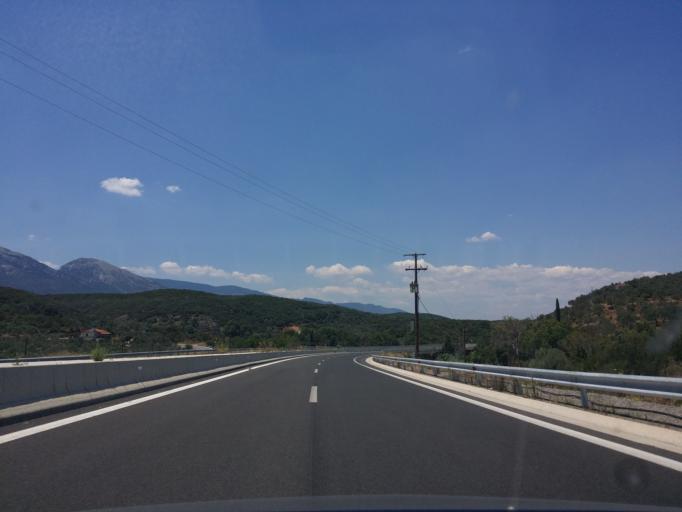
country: GR
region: Peloponnese
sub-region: Nomos Lakonias
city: Magoula
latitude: 37.1282
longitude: 22.4029
